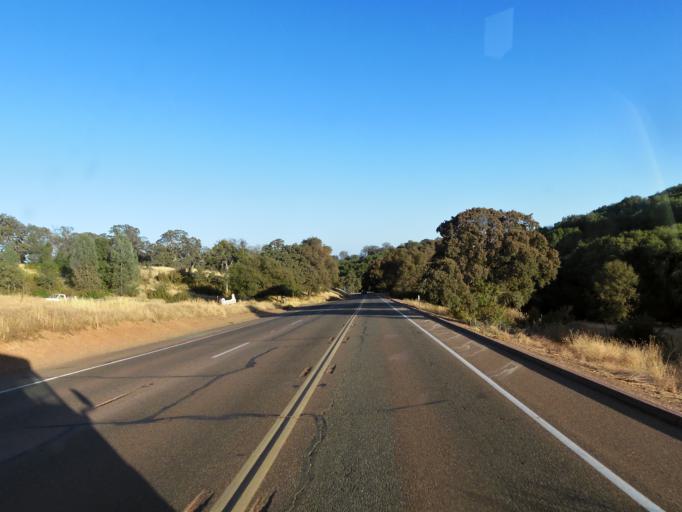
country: US
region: California
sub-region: Mariposa County
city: Mariposa
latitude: 37.4742
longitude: -119.9722
